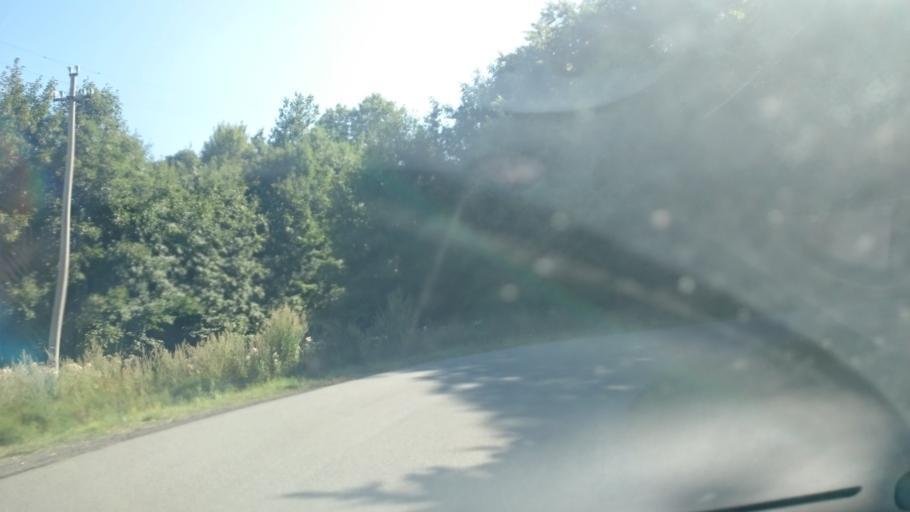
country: IT
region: Emilia-Romagna
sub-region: Provincia di Reggio Emilia
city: Villa Minozzo
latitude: 44.2999
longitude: 10.4299
